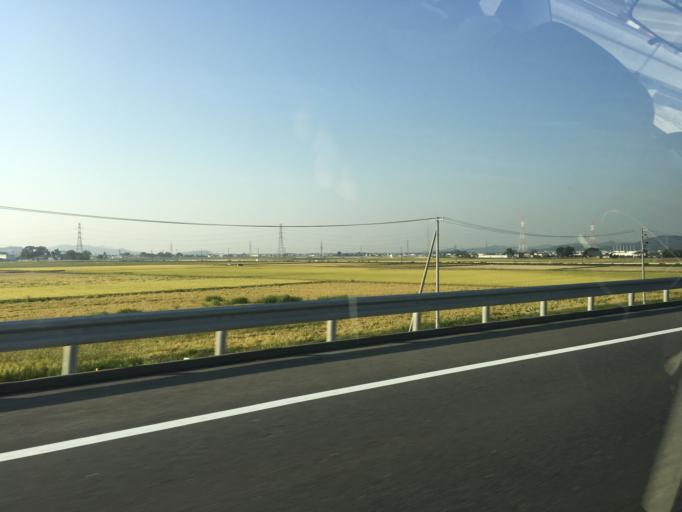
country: JP
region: Miyagi
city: Ishinomaki
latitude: 38.4606
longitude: 141.2792
